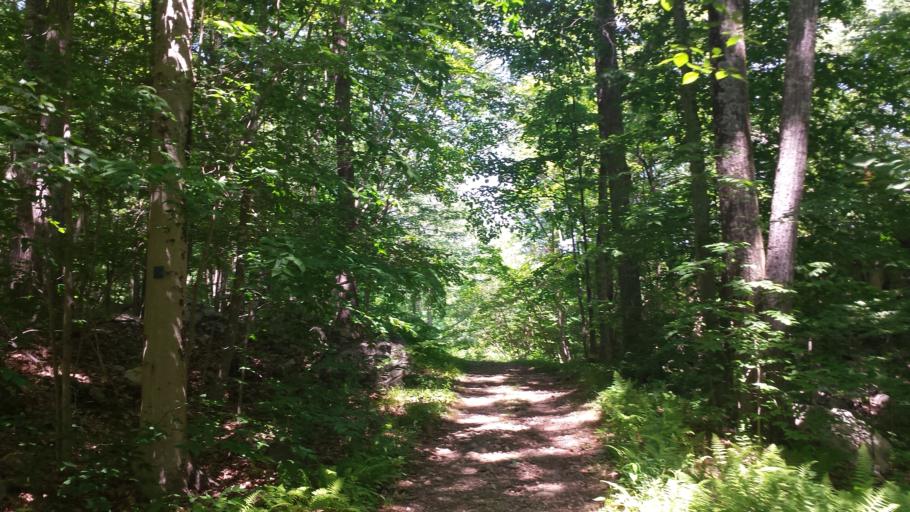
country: US
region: New York
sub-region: Westchester County
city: Pound Ridge
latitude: 41.2581
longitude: -73.5763
